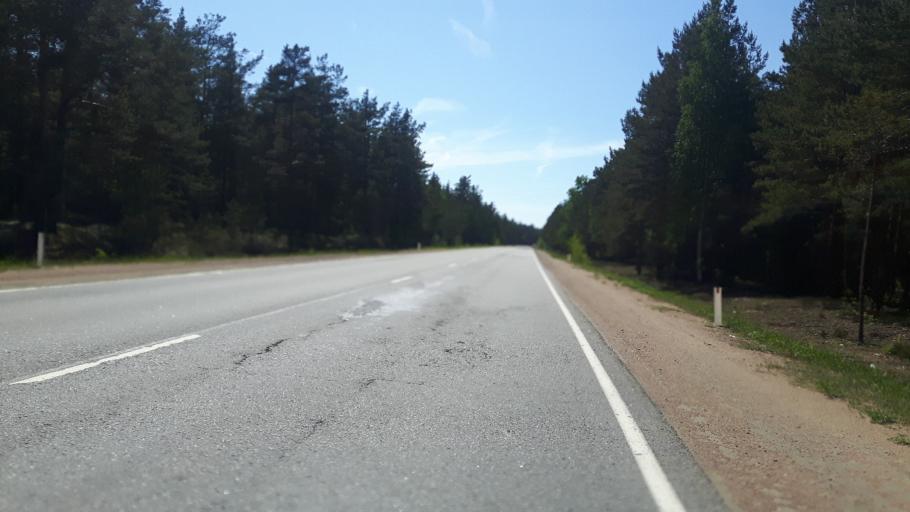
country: RU
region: Leningrad
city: Sista-Palkino
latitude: 59.7684
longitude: 28.7604
